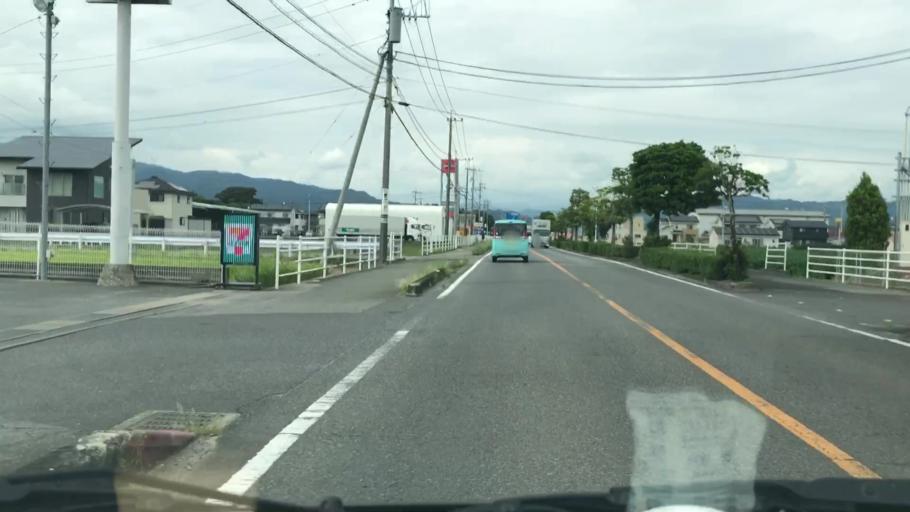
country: JP
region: Saga Prefecture
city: Saga-shi
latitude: 33.2730
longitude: 130.2610
